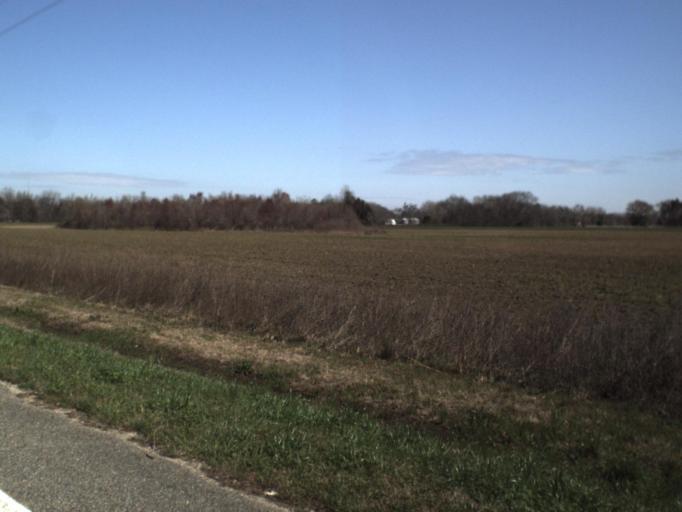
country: US
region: Florida
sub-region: Calhoun County
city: Blountstown
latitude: 30.5691
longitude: -85.0217
